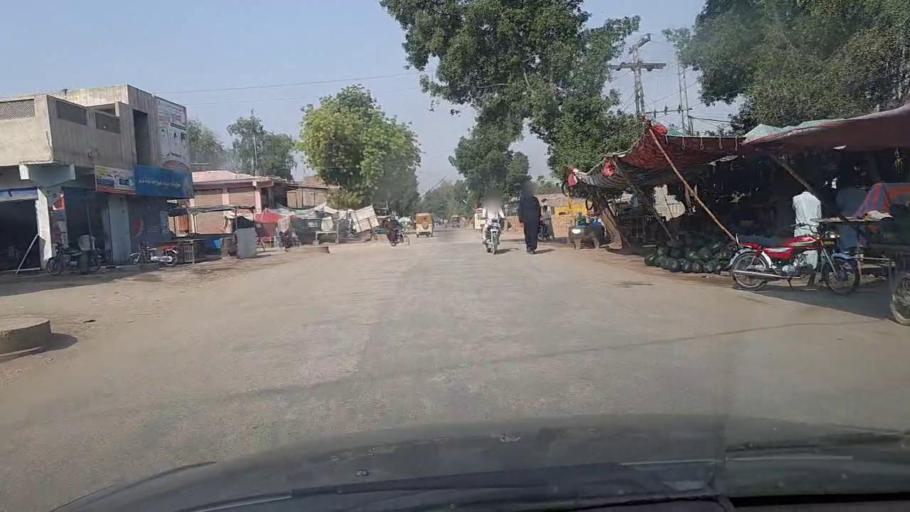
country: PK
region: Sindh
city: Mirpur Mathelo
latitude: 28.0241
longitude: 69.5610
